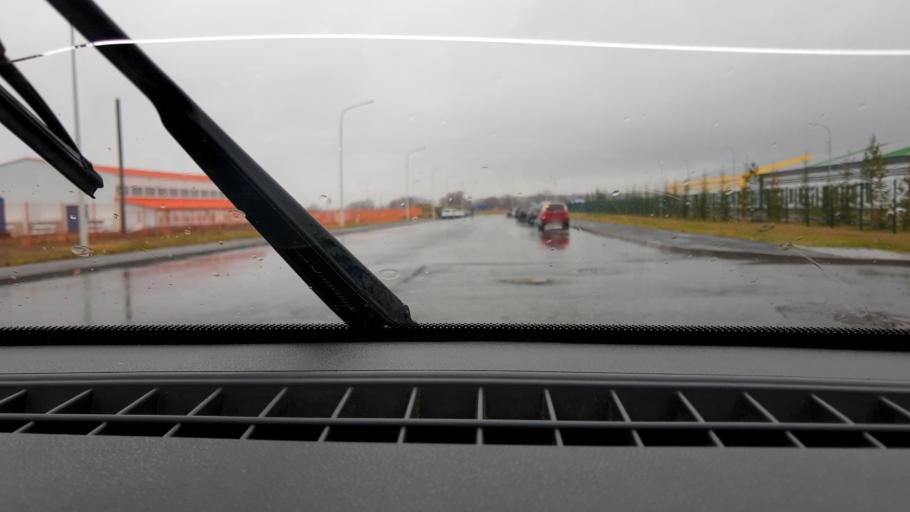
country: RU
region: Bashkortostan
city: Ufa
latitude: 54.6031
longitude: 55.9074
